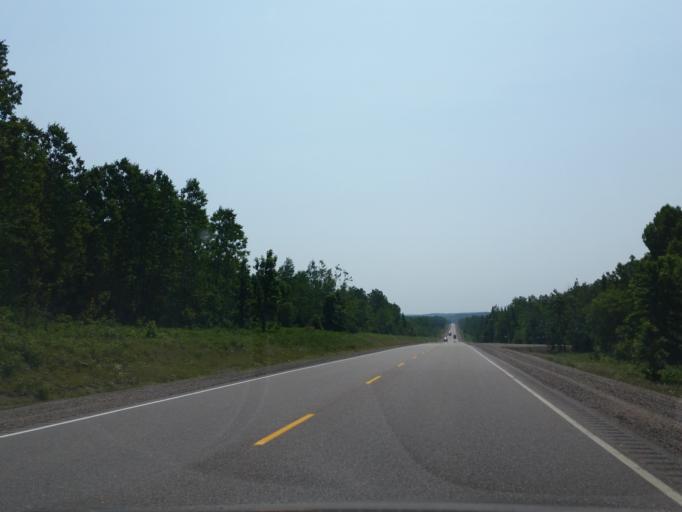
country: CA
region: Ontario
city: Mattawa
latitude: 46.2798
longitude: -78.3805
